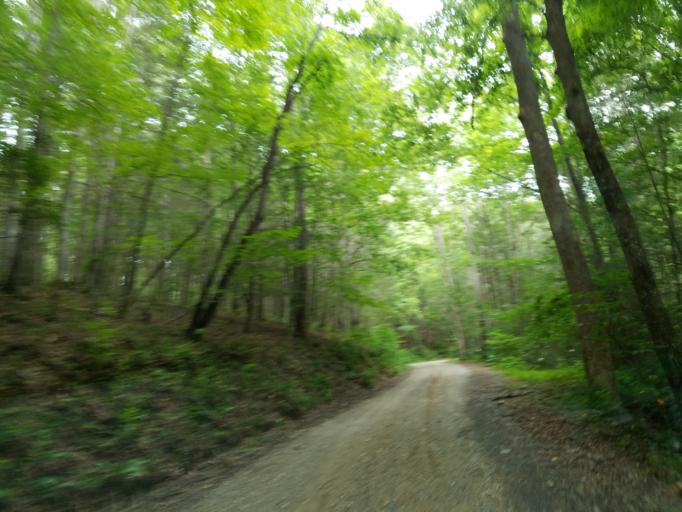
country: US
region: Georgia
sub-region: Union County
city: Blairsville
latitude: 34.7711
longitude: -84.0630
